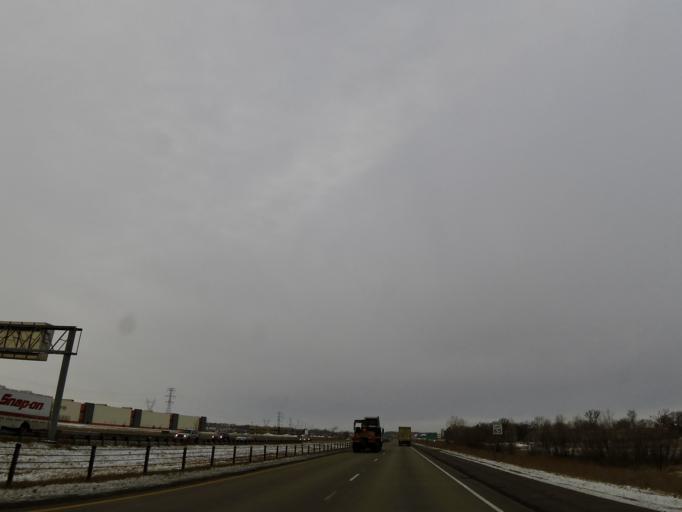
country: US
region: Minnesota
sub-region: Hennepin County
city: Eden Prairie
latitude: 44.7834
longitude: -93.4520
